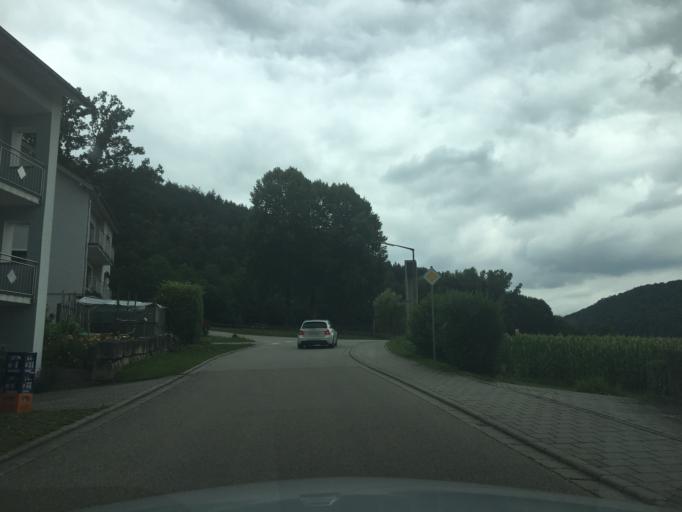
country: DE
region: Bavaria
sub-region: Regierungsbezirk Mittelfranken
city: Greding
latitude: 48.9961
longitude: 11.3594
